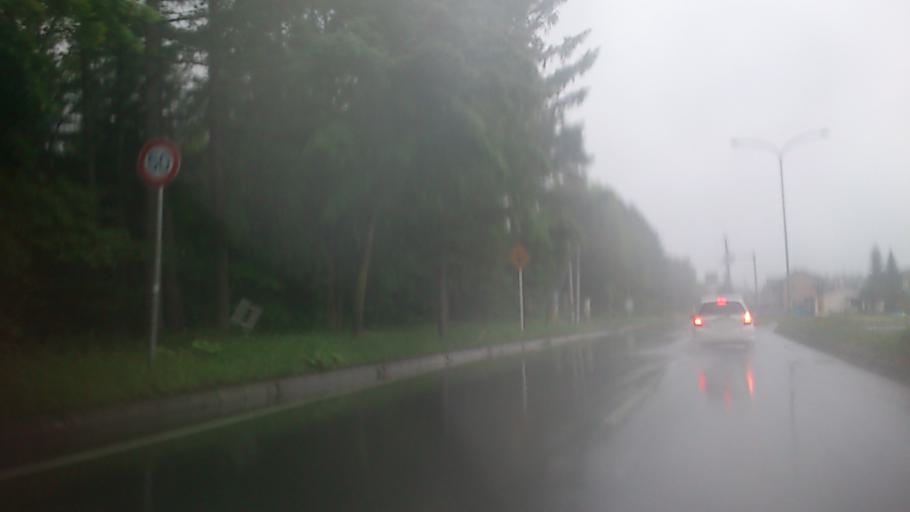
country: JP
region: Hokkaido
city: Obihiro
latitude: 42.9071
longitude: 143.1334
